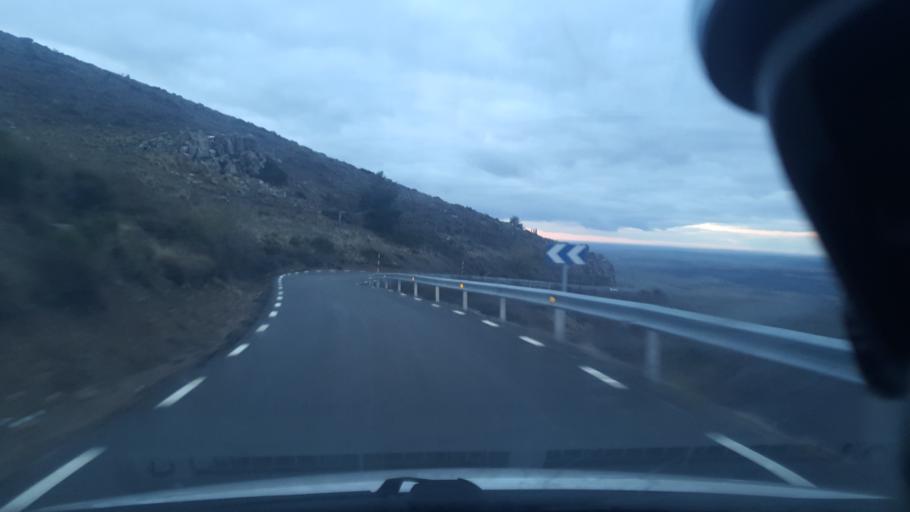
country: ES
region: Castille and Leon
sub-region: Provincia de Avila
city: Ojos-Albos
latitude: 40.7193
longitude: -4.4504
